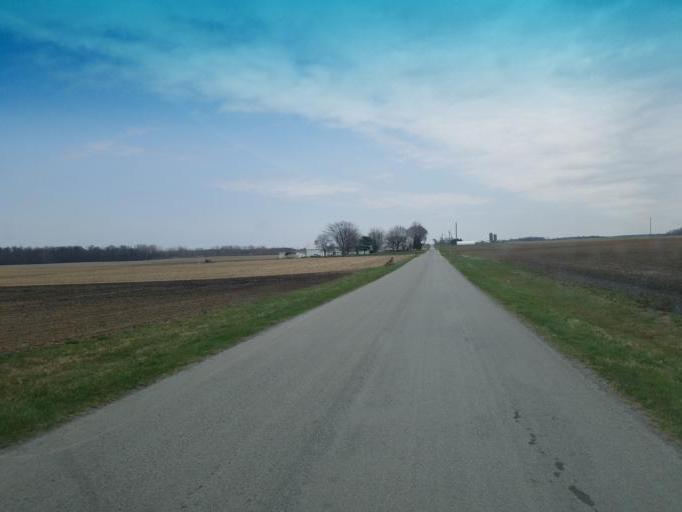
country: US
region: Ohio
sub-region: Wyandot County
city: Upper Sandusky
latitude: 40.8621
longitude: -83.2189
